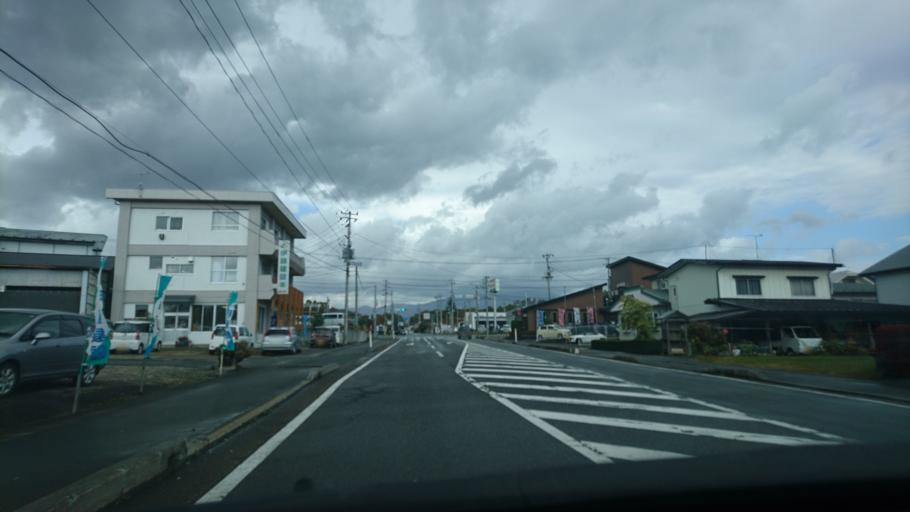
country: JP
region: Iwate
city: Shizukuishi
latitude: 39.6970
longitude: 141.0230
